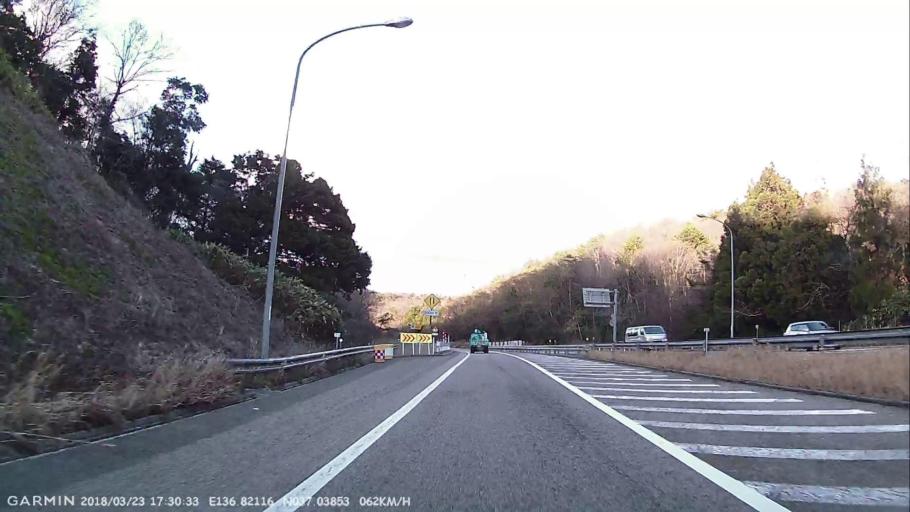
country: JP
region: Ishikawa
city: Nanao
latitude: 37.0386
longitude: 136.8213
